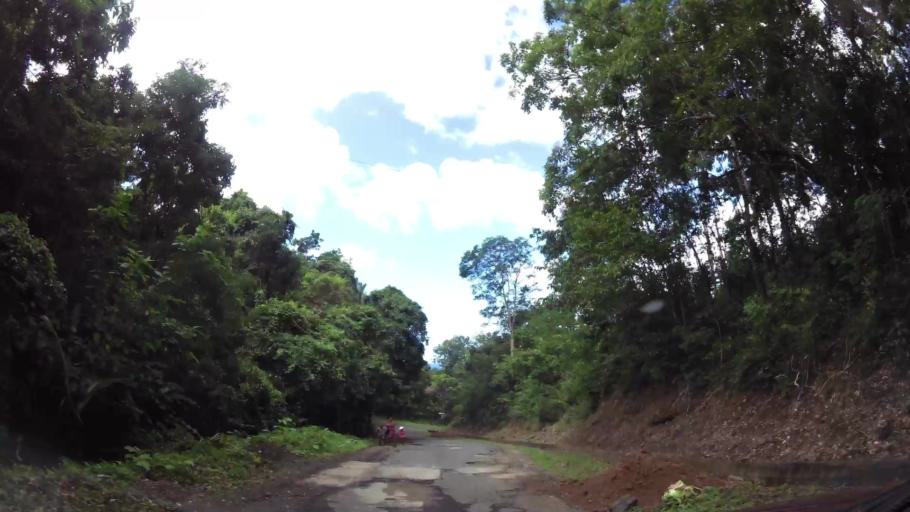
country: DM
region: Saint John
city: Portsmouth
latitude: 15.6180
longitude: -61.4634
